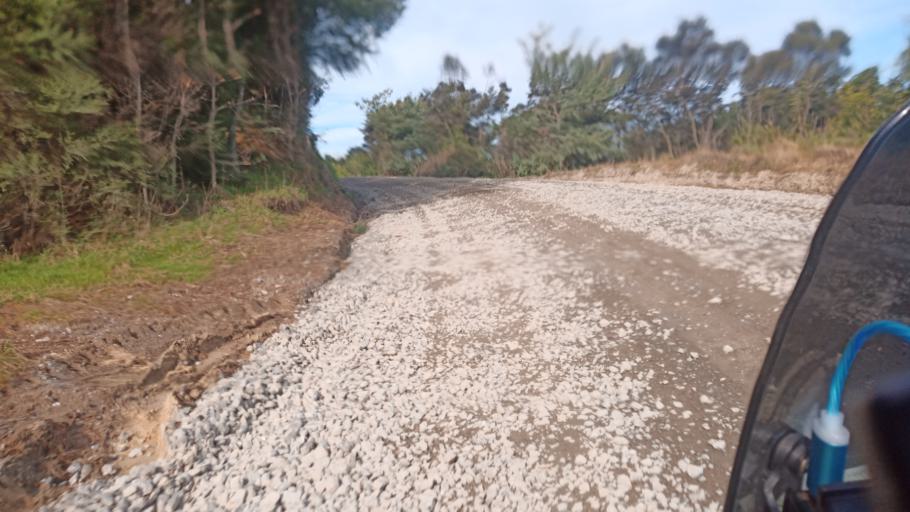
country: NZ
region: Gisborne
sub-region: Gisborne District
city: Gisborne
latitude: -38.1312
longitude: 178.1884
